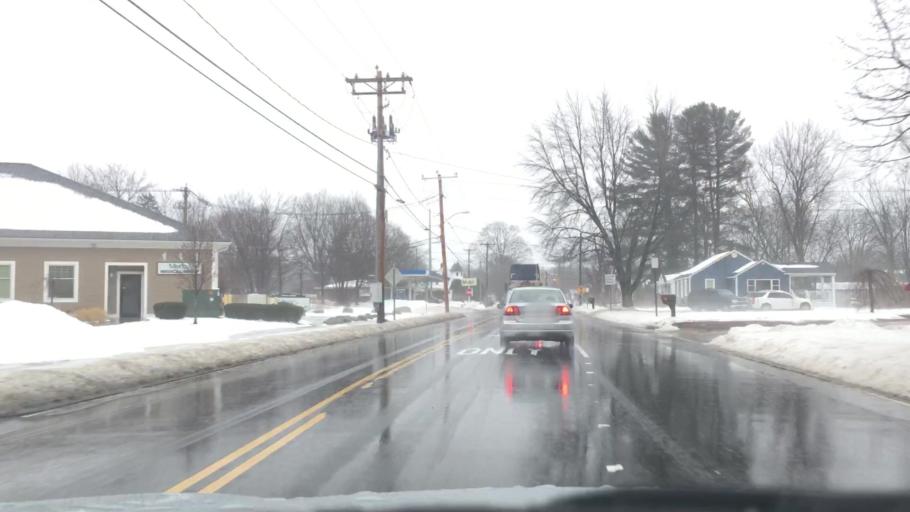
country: US
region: Massachusetts
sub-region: Hampden County
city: Ludlow
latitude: 42.1824
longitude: -72.5077
